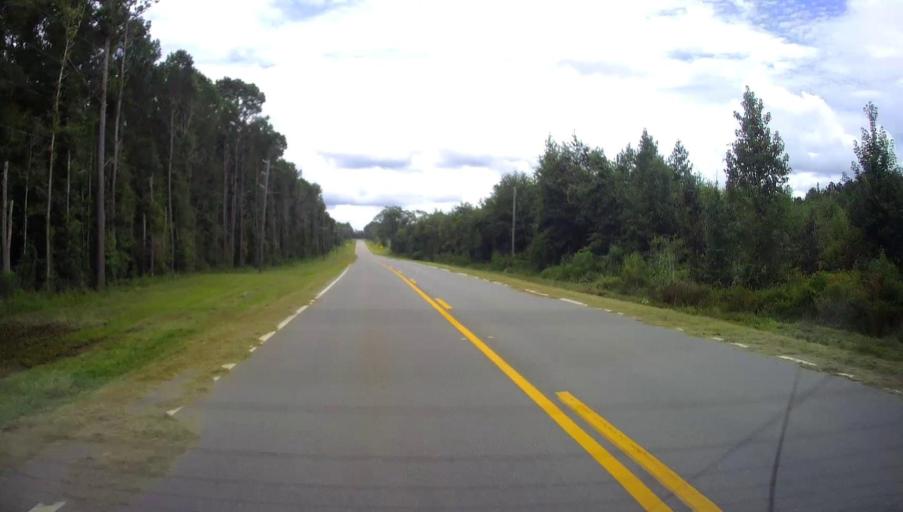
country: US
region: Georgia
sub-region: Schley County
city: Ellaville
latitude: 32.2632
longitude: -84.1978
